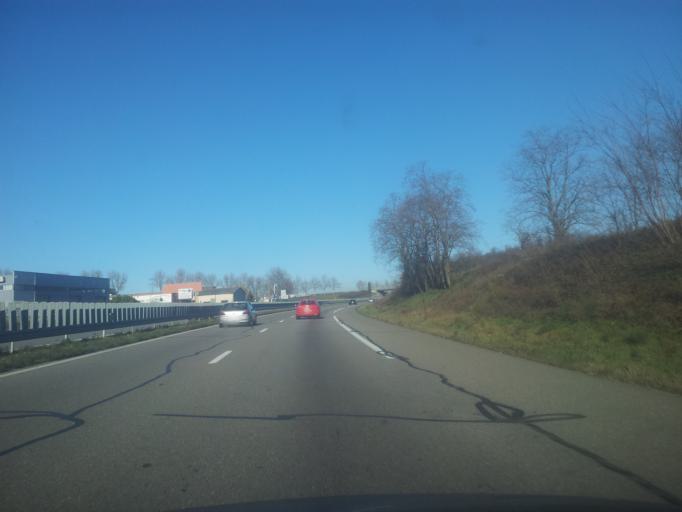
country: FR
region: Rhone-Alpes
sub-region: Departement de la Drome
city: Saint-Marcel-les-Valence
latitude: 44.9747
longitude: 4.9648
